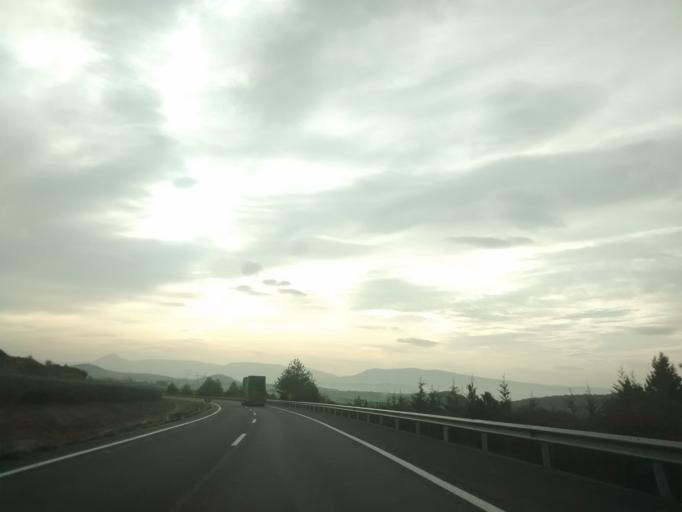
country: ES
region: Navarre
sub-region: Provincia de Navarra
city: Oltza
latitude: 42.8833
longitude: -1.7659
